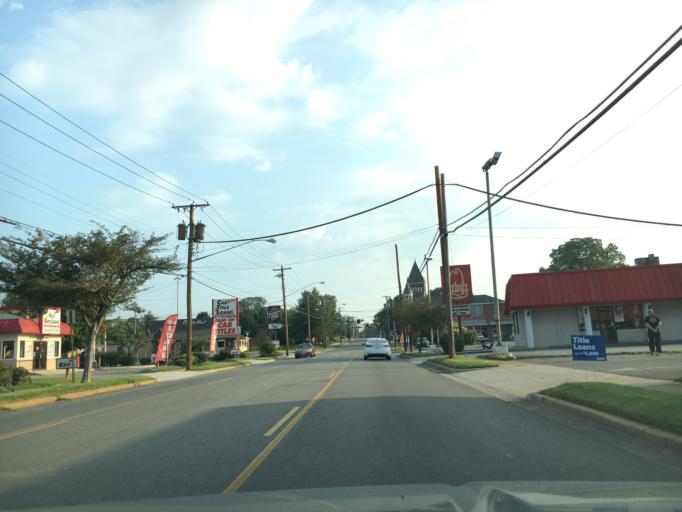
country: US
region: Virginia
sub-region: City of Lynchburg
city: West Lynchburg
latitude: 37.4014
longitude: -79.1681
